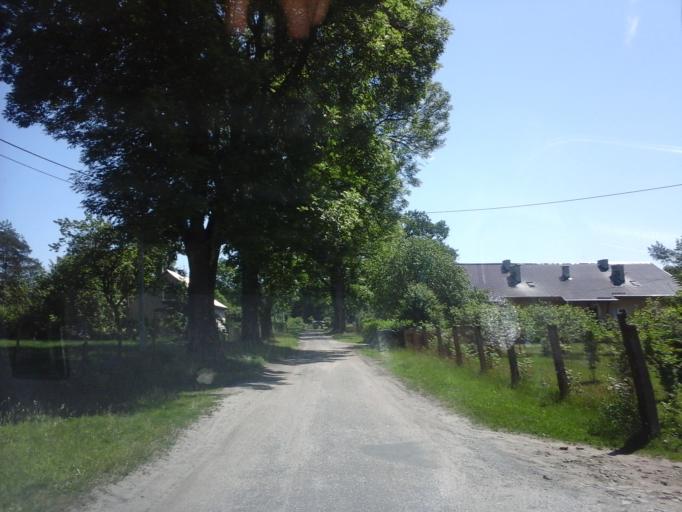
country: PL
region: West Pomeranian Voivodeship
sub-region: Powiat walecki
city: Tuczno
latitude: 53.2215
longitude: 16.0544
